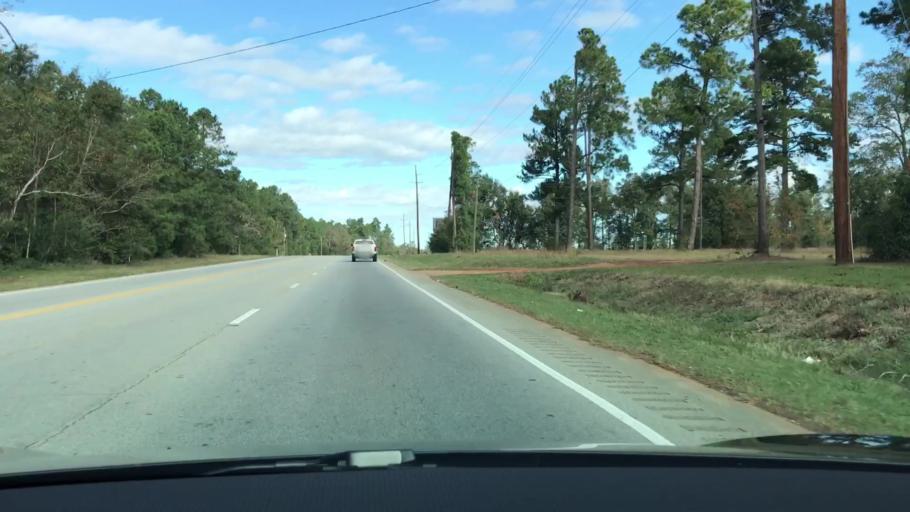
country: US
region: Georgia
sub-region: Jefferson County
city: Louisville
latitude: 33.0331
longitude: -82.4054
